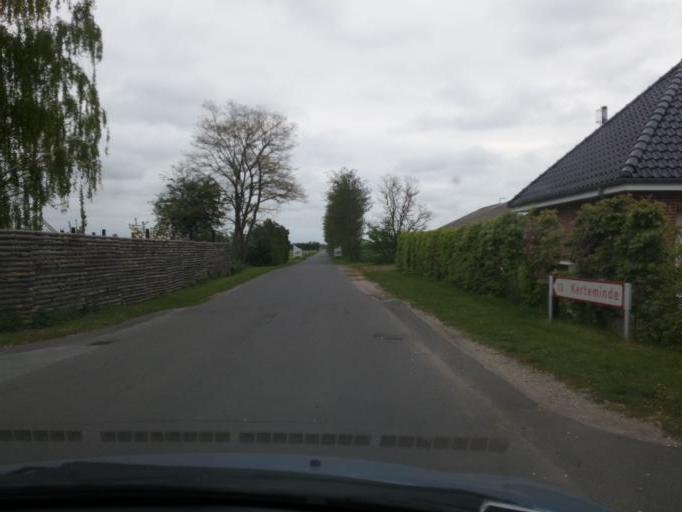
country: DK
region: South Denmark
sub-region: Odense Kommune
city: Bullerup
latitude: 55.4086
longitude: 10.5125
